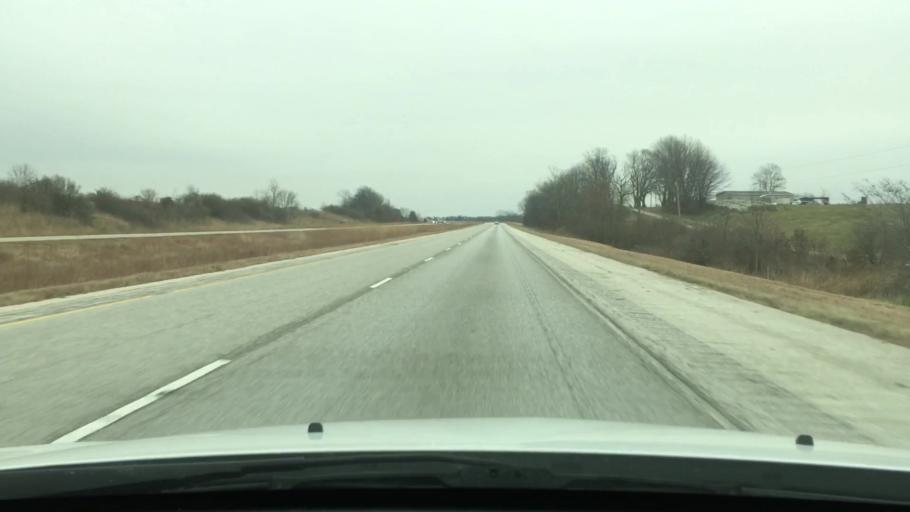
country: US
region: Illinois
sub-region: Morgan County
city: South Jacksonville
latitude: 39.6803
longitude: -90.2763
